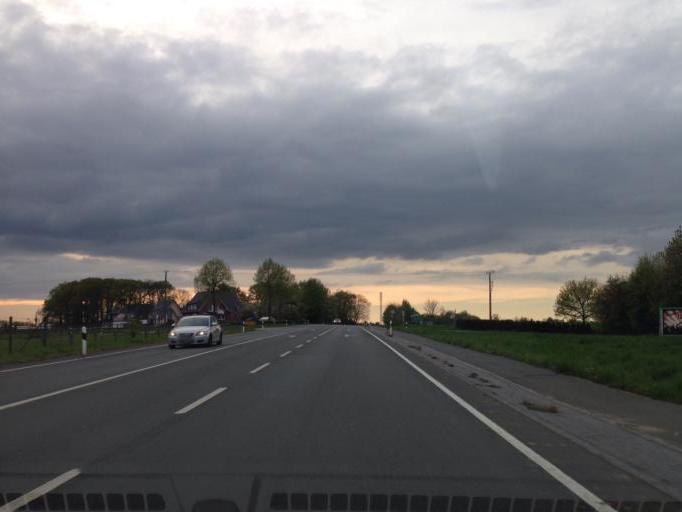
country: DE
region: North Rhine-Westphalia
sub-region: Regierungsbezirk Munster
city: Altenberge
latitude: 52.0199
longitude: 7.5025
